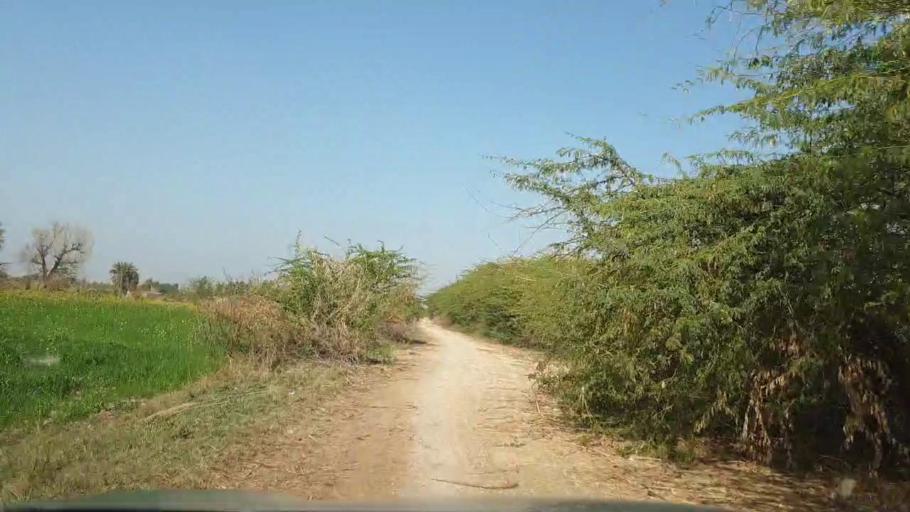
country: PK
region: Sindh
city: Berani
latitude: 25.6825
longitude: 68.8956
